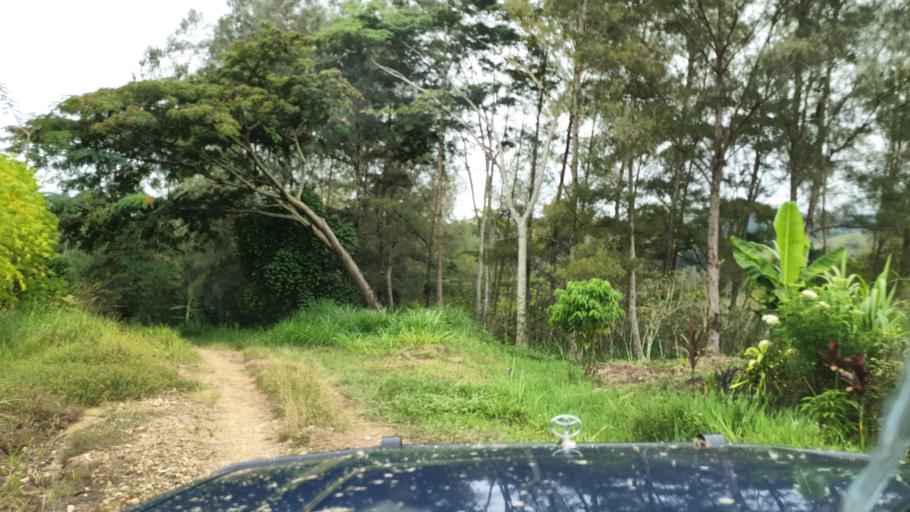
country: PG
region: Jiwaka
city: Minj
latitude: -5.9296
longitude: 144.7481
